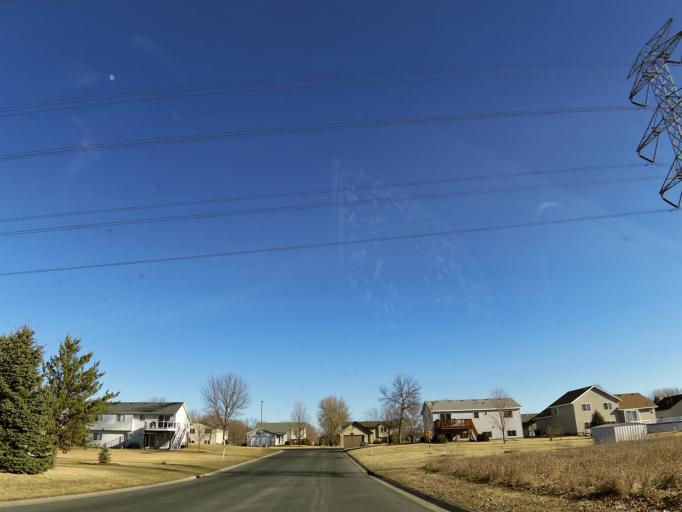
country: US
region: Minnesota
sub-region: Scott County
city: Savage
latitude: 44.7760
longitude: -93.3942
